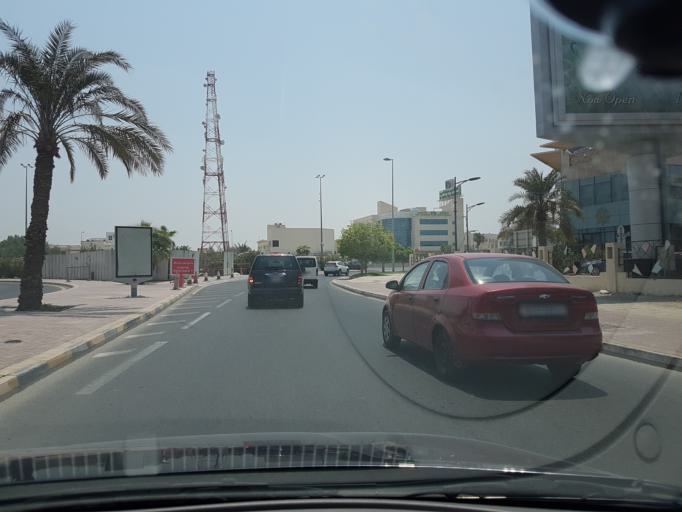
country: BH
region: Manama
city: Manama
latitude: 26.2048
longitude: 50.5756
